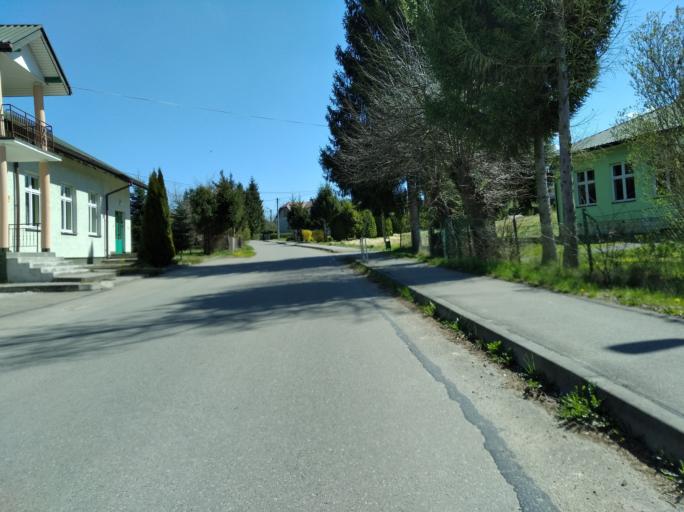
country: PL
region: Subcarpathian Voivodeship
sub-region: Powiat brzozowski
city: Dydnia
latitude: 49.6922
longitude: 22.2215
